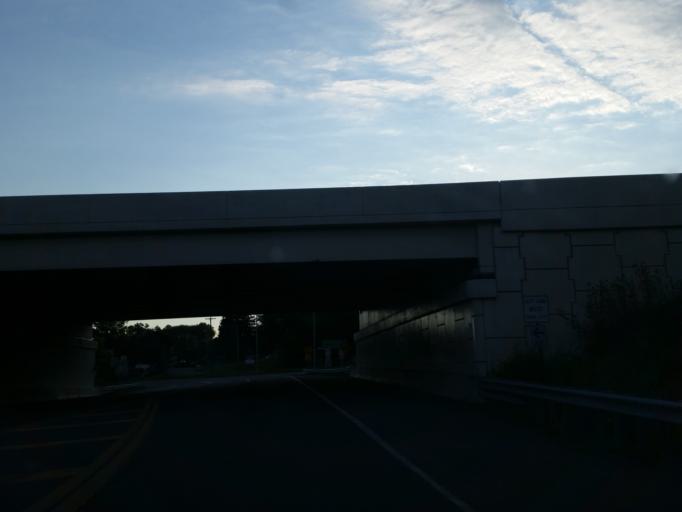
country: US
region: Pennsylvania
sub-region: Lancaster County
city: Adamstown
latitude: 40.2491
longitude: -76.0364
